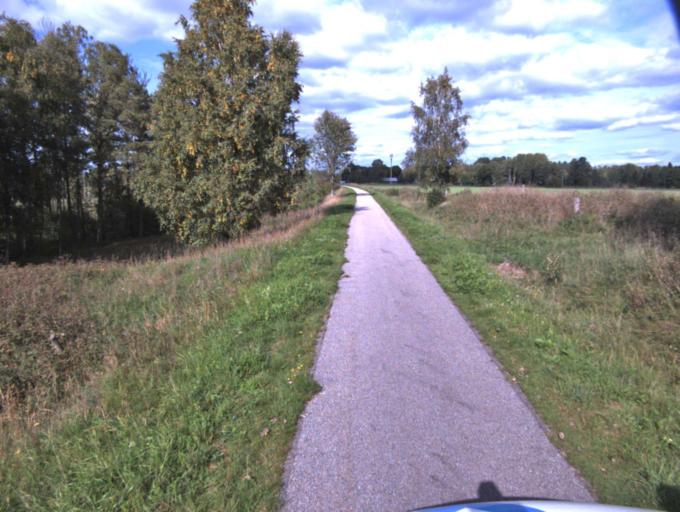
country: SE
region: Vaestra Goetaland
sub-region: Ulricehamns Kommun
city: Ulricehamn
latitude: 57.8517
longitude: 13.4266
